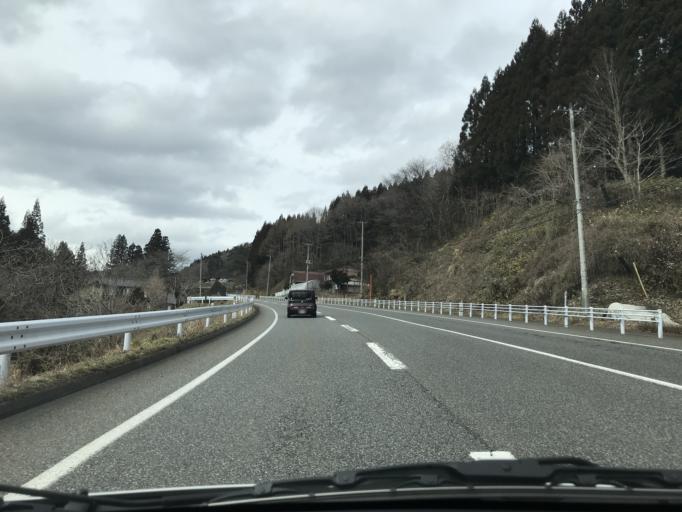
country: JP
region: Iwate
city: Tono
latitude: 39.3374
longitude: 141.4443
